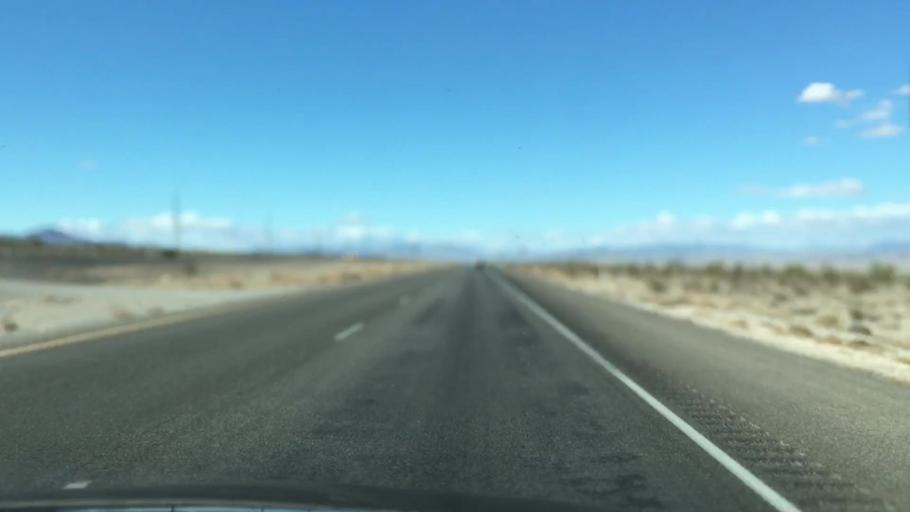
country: US
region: Nevada
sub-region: Clark County
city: Summerlin South
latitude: 36.4797
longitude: -115.4713
